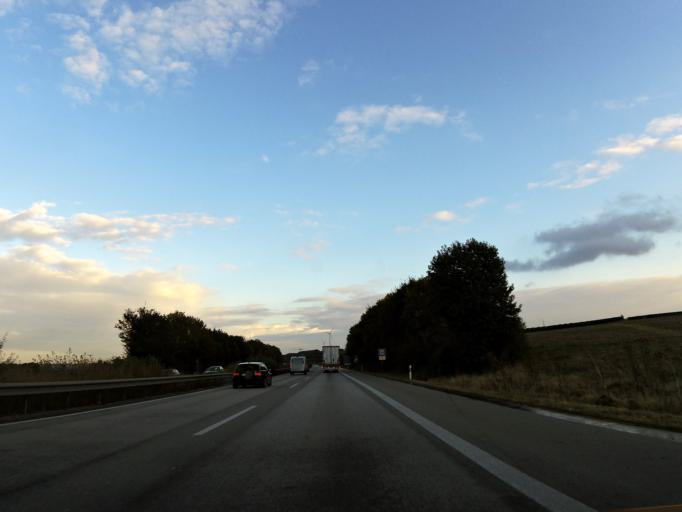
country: DE
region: Rheinland-Pfalz
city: Sprendlingen
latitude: 49.8439
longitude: 7.9874
